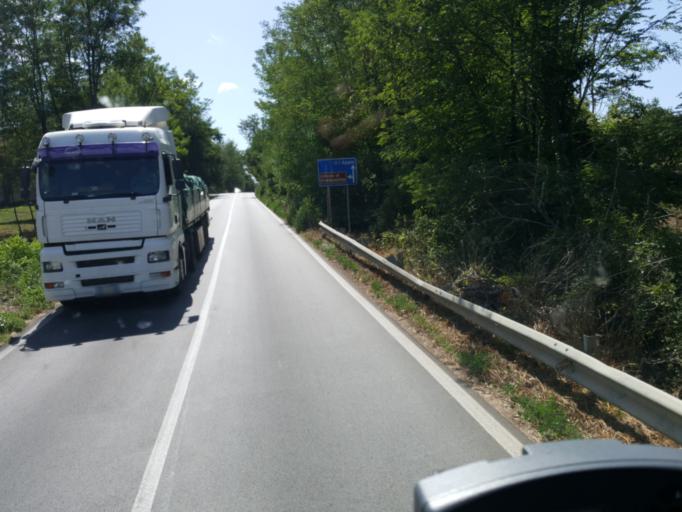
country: IT
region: Latium
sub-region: Provincia di Latina
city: Priverno
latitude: 41.4391
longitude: 13.1942
